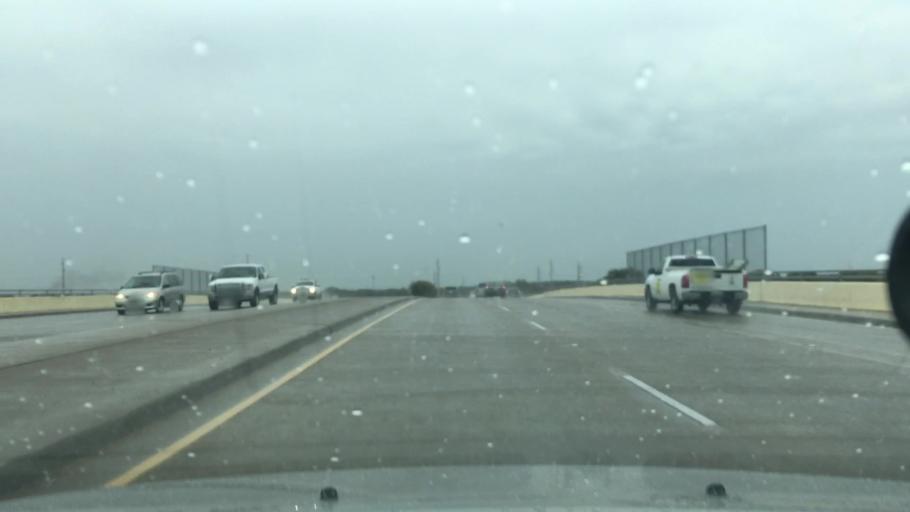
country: US
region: Texas
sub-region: Denton County
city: Denton
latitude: 33.2343
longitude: -97.0968
